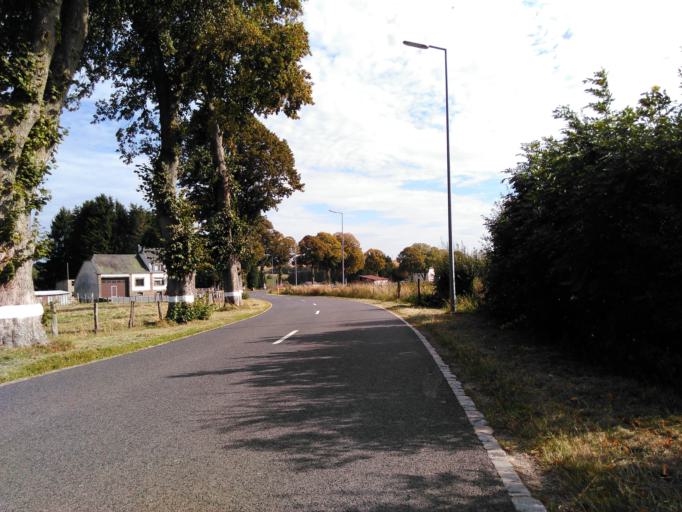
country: LU
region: Diekirch
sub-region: Canton de Clervaux
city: Troisvierges
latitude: 50.1492
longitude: 5.9795
